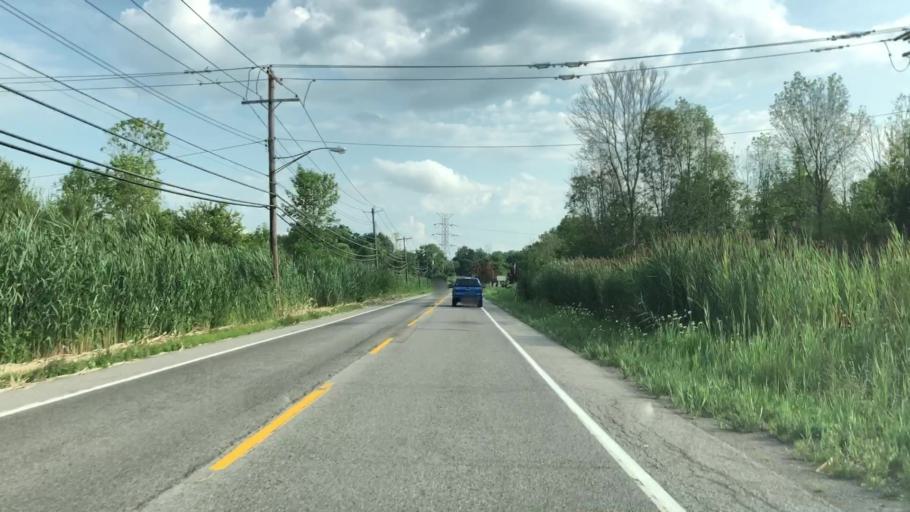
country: US
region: New York
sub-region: Erie County
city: Elma Center
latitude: 42.8334
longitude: -78.6368
